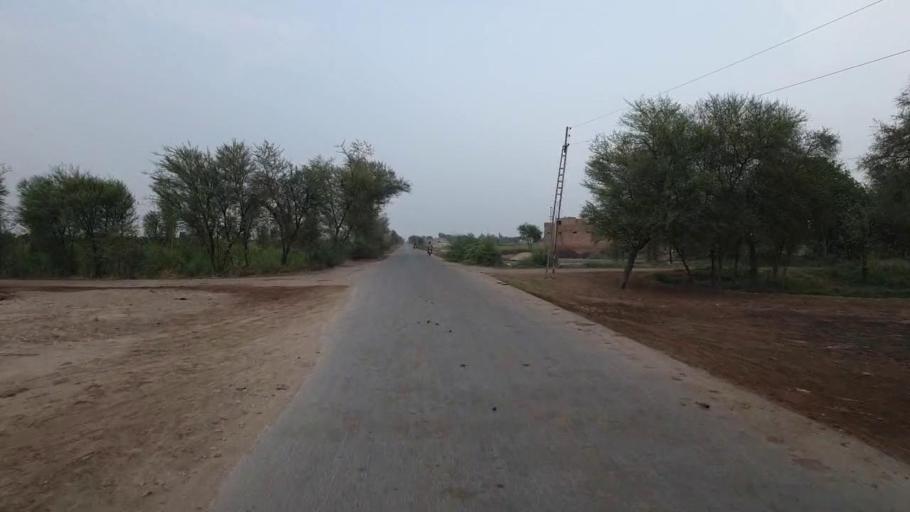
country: PK
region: Sindh
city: Daur
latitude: 26.4111
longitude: 68.2365
